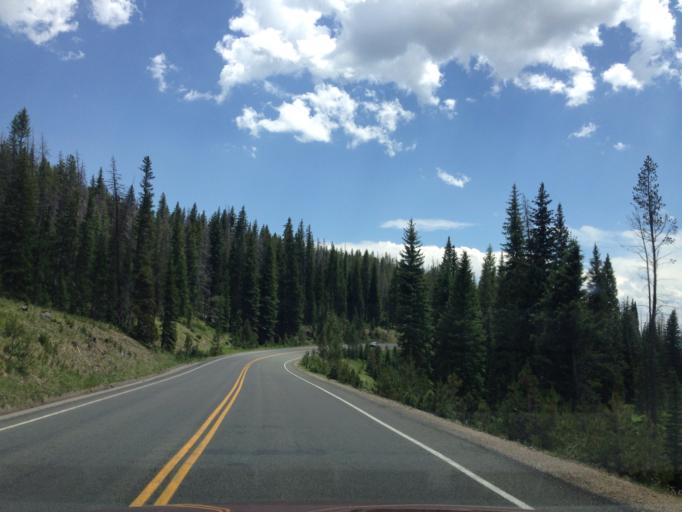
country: US
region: Colorado
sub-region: Grand County
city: Granby
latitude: 40.3430
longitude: -105.8576
